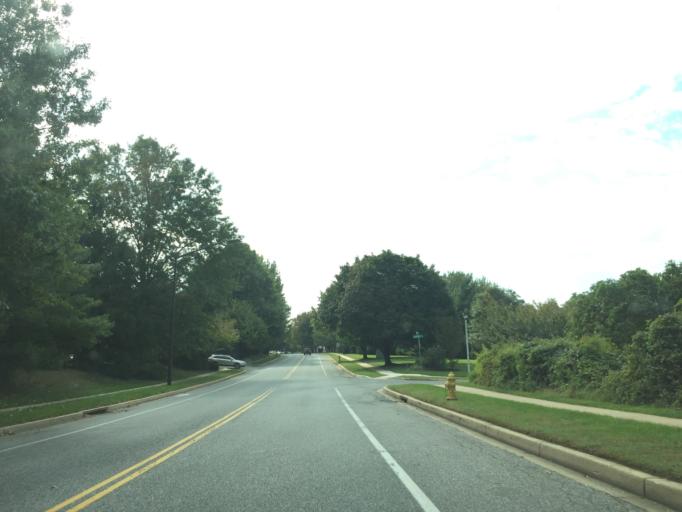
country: US
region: Maryland
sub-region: Harford County
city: Bel Air South
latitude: 39.4944
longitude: -76.3312
